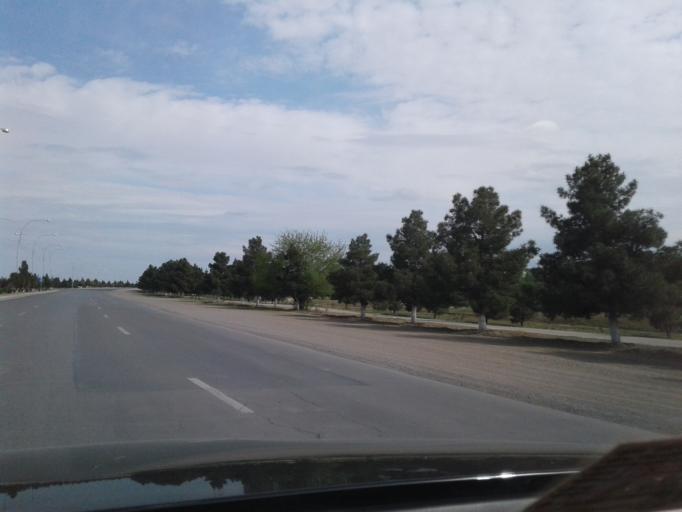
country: TM
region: Ahal
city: Ashgabat
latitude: 37.9701
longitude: 58.2958
